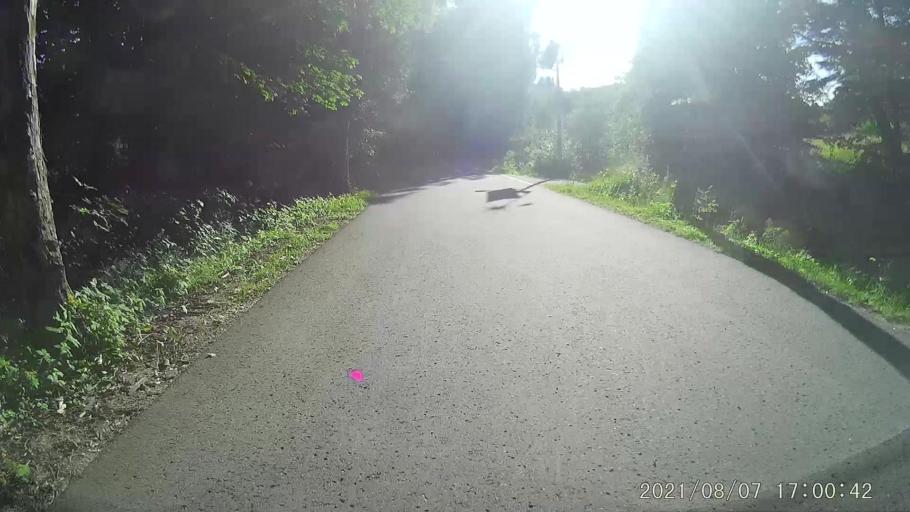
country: PL
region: Lower Silesian Voivodeship
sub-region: Powiat klodzki
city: Bystrzyca Klodzka
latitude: 50.2887
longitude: 16.5490
